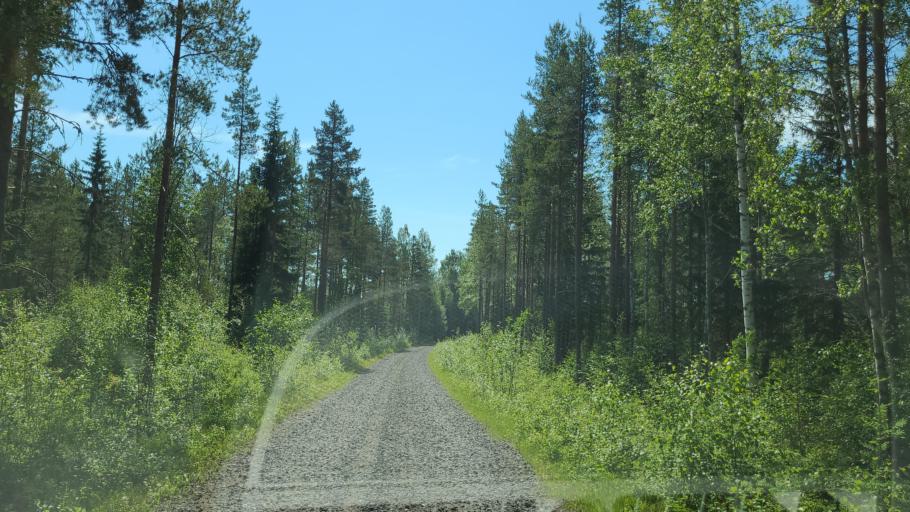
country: SE
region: Vaesterbotten
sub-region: Robertsfors Kommun
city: Robertsfors
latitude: 64.0956
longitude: 20.8343
